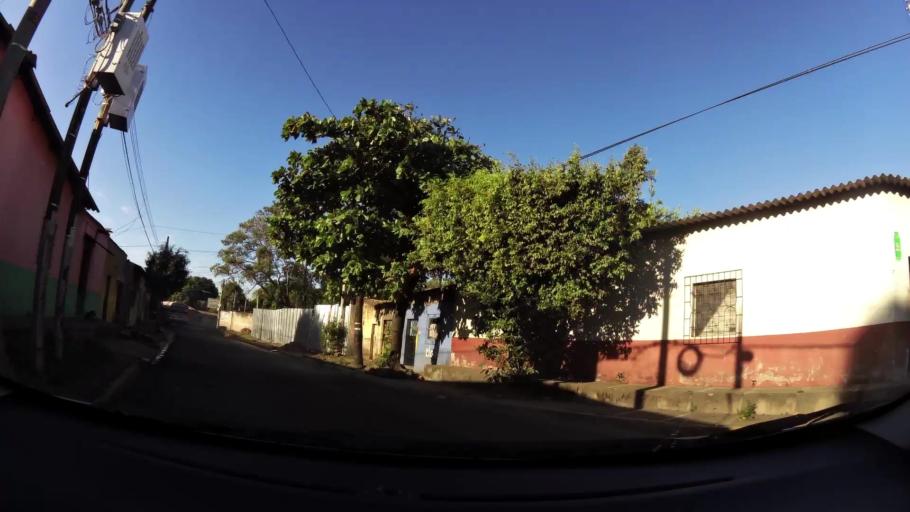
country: SV
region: Sonsonate
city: San Antonio del Monte
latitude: 13.7176
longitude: -89.7327
